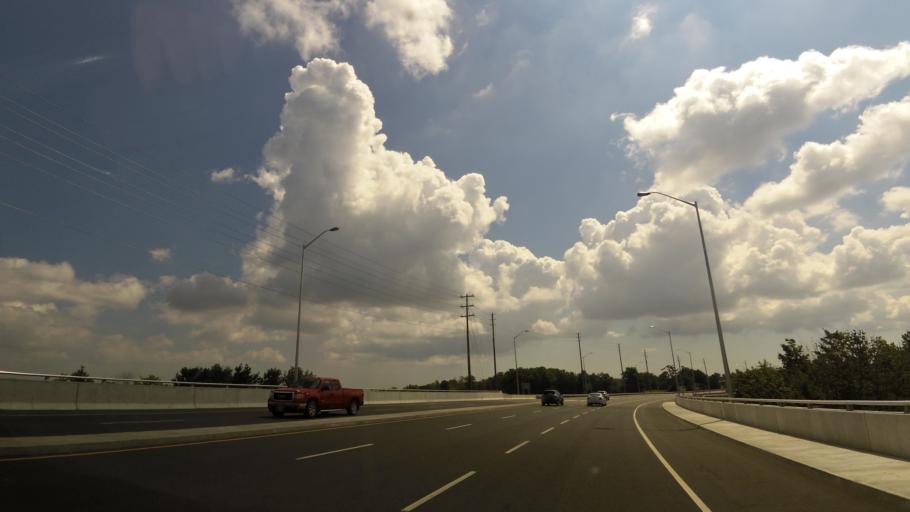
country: CA
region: Ontario
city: Pickering
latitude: 43.9153
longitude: -79.0952
